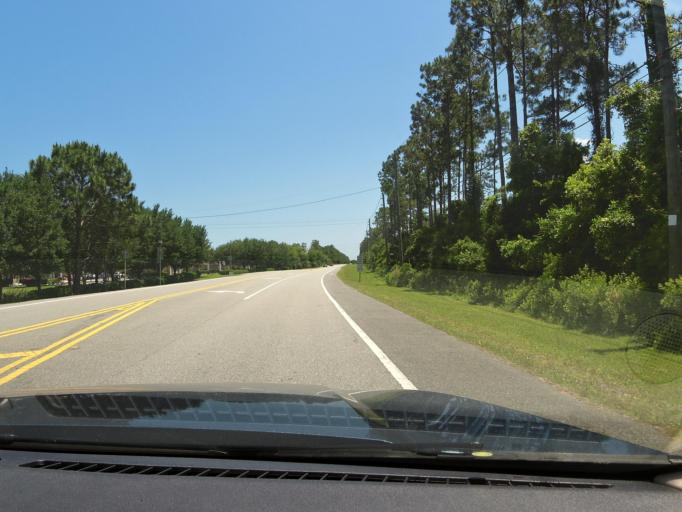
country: US
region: Florida
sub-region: Flagler County
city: Flagler Beach
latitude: 29.4712
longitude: -81.1755
